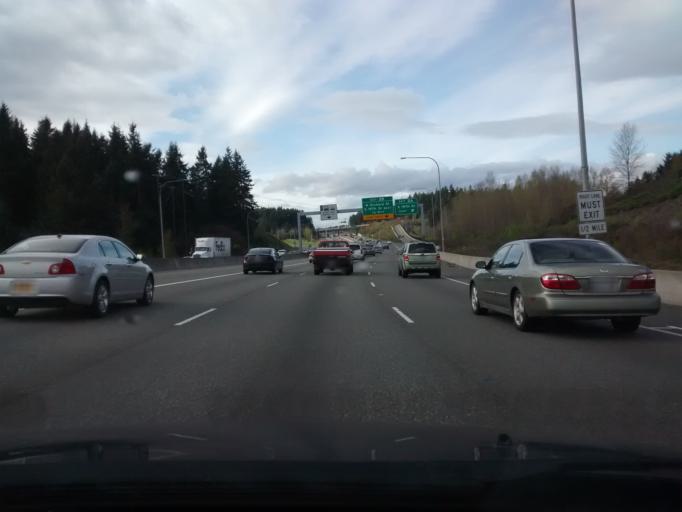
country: US
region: Washington
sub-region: Pierce County
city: Fircrest
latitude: 47.2366
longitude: -122.4996
